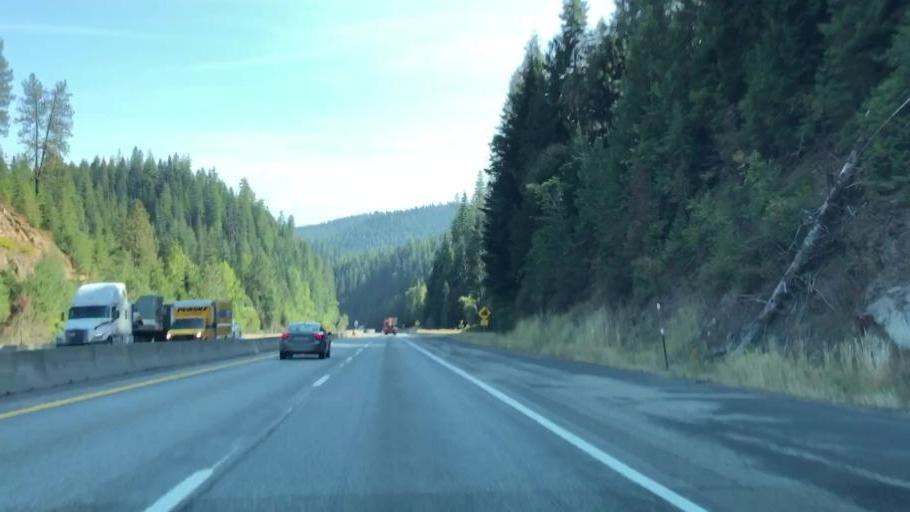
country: US
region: Idaho
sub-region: Shoshone County
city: Pinehurst
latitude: 47.6039
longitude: -116.5000
